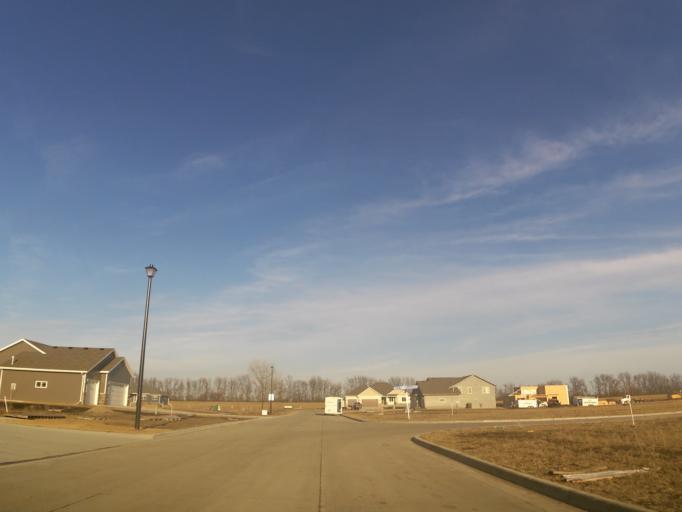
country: US
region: North Dakota
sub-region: Grand Forks County
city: Grand Forks
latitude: 47.8640
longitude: -97.0269
